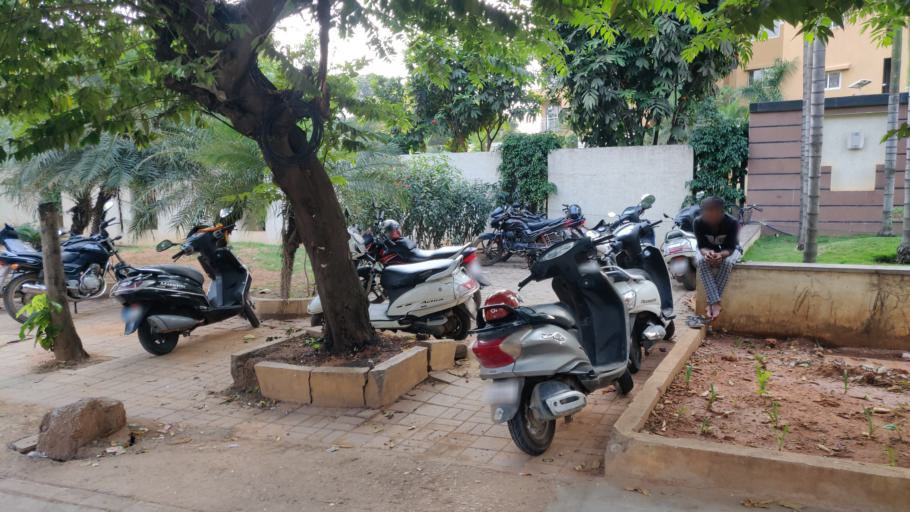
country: IN
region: Karnataka
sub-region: Bangalore Urban
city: Yelahanka
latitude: 13.1171
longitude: 77.5779
